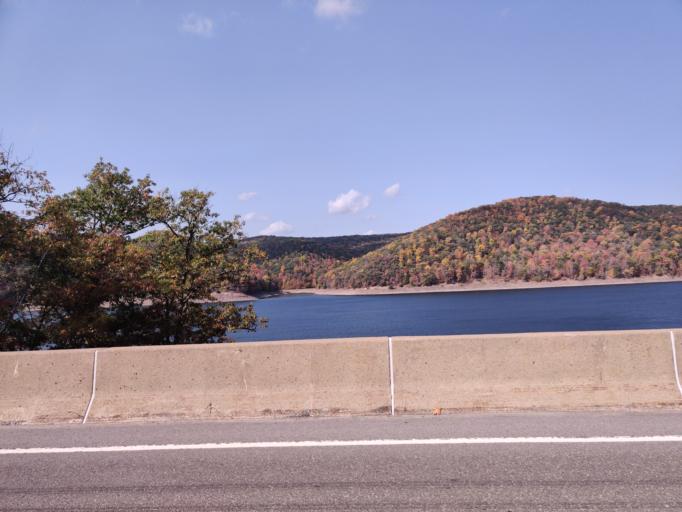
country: US
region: Pennsylvania
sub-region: Warren County
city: Sheffield
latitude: 41.8568
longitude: -78.9750
